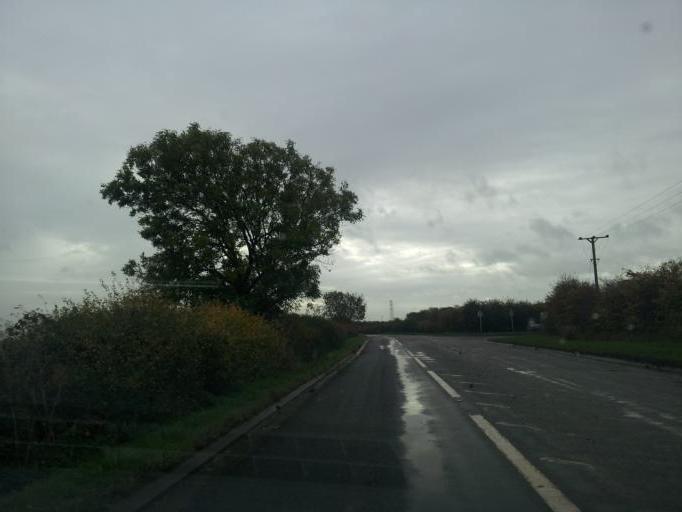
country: GB
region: England
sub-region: Nottinghamshire
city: Newark on Trent
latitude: 53.0258
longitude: -0.8025
